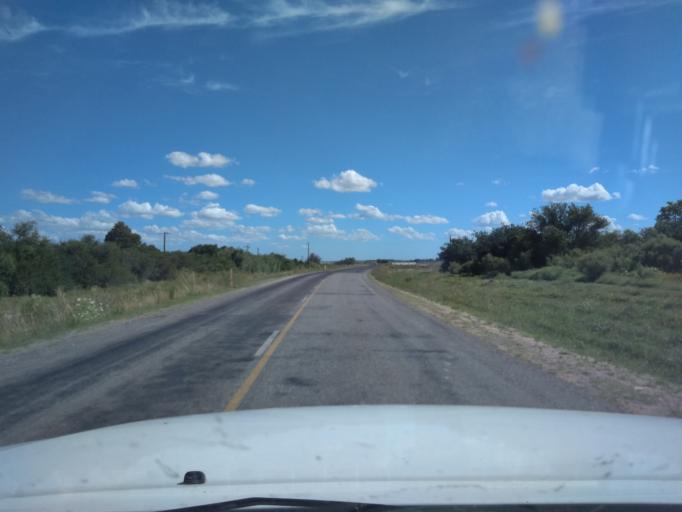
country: UY
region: Canelones
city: San Ramon
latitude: -34.2665
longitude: -55.9293
